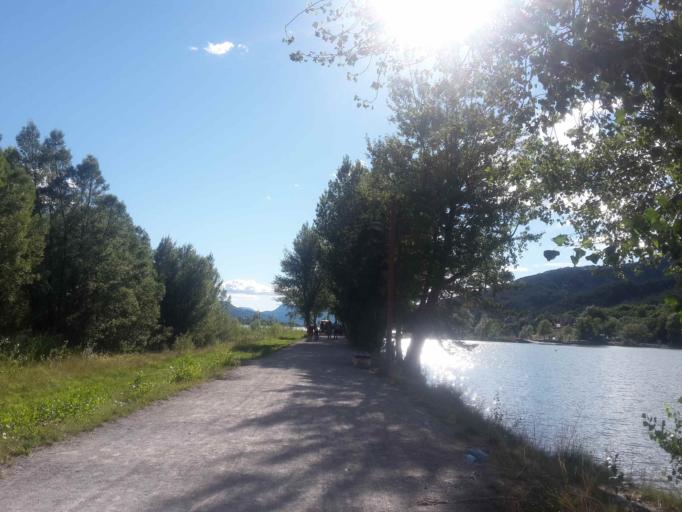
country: FR
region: Provence-Alpes-Cote d'Azur
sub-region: Departement des Hautes-Alpes
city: Embrun
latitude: 44.5469
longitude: 6.4706
